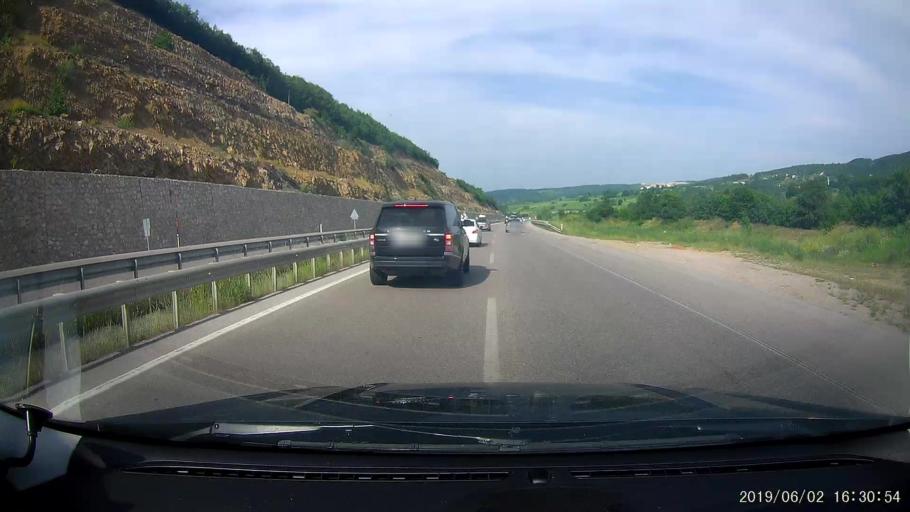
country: TR
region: Samsun
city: Ladik
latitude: 41.0290
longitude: 35.8916
